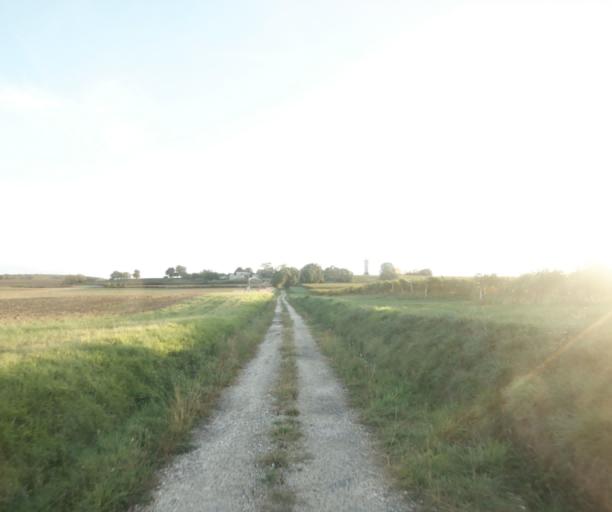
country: FR
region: Midi-Pyrenees
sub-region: Departement du Gers
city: Gondrin
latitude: 43.8495
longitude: 0.2577
